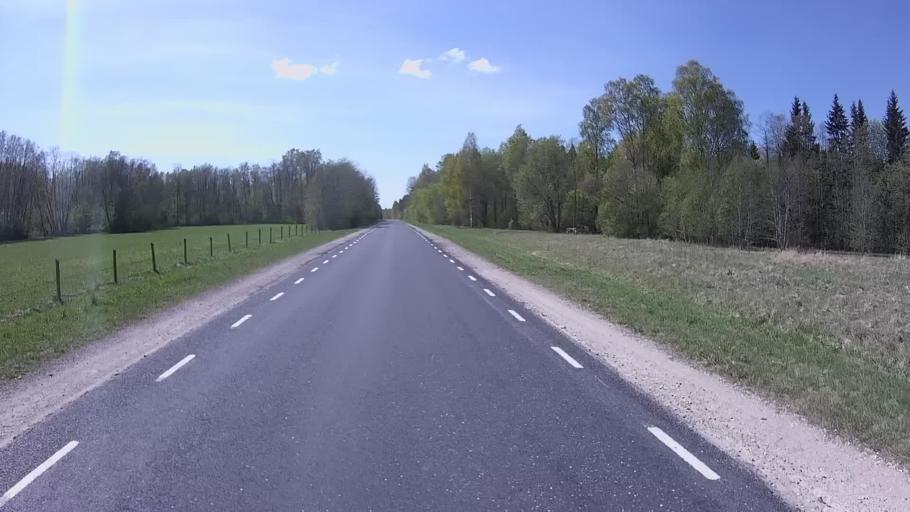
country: EE
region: Laeaene
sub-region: Ridala Parish
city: Uuemoisa
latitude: 59.0286
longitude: 23.8145
